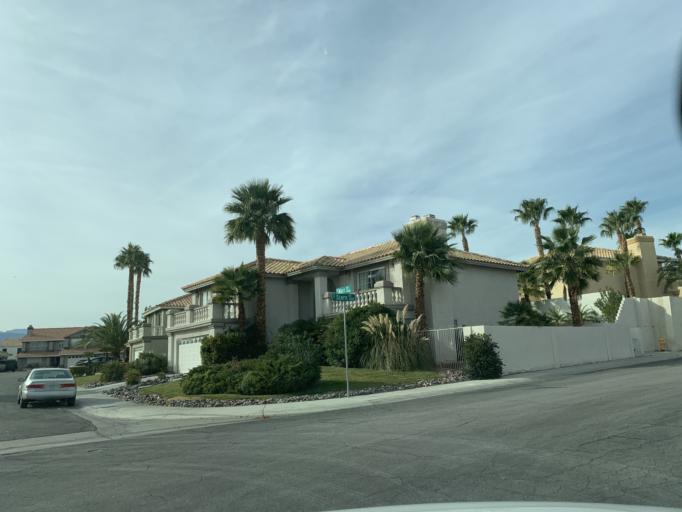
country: US
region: Nevada
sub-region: Clark County
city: Summerlin South
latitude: 36.1359
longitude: -115.3005
